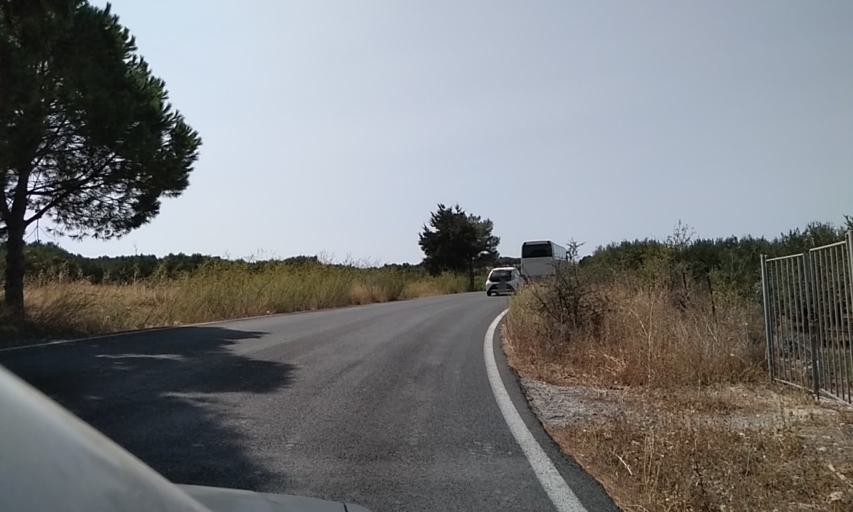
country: GR
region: Crete
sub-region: Nomos Lasithiou
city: Makry-Gialos
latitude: 35.1005
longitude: 26.0601
